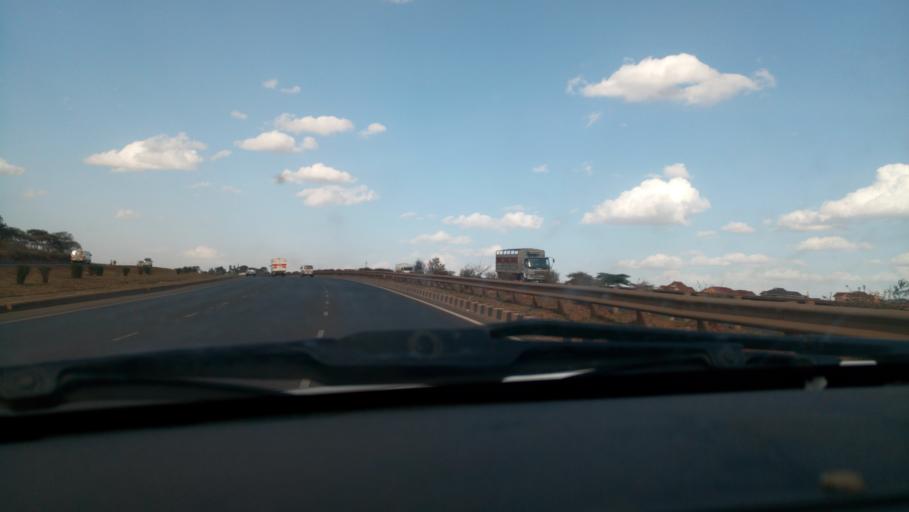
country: KE
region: Nairobi Area
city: Thika
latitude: -1.1290
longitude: 36.9973
